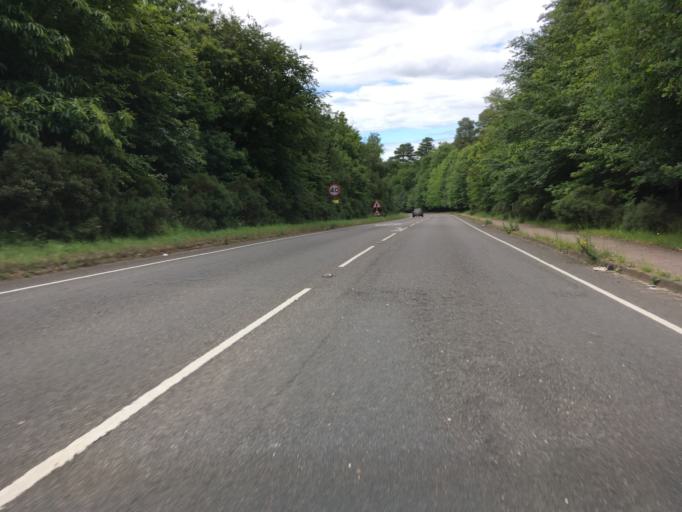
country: GB
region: England
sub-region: Central Bedfordshire
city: Aspley Guise
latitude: 52.0039
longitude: -0.6435
